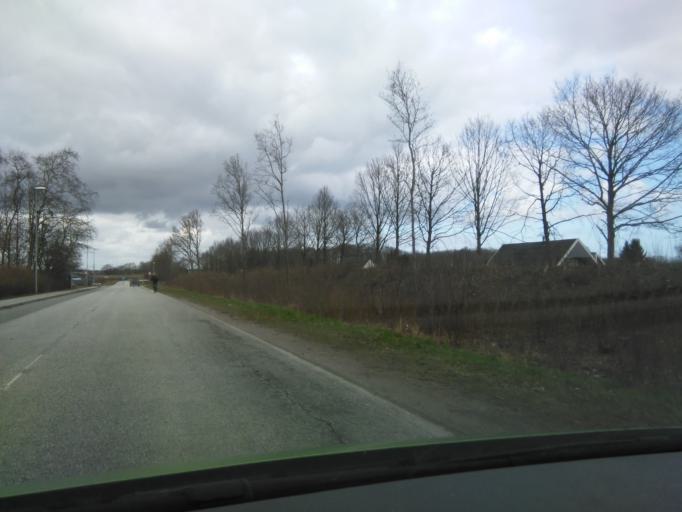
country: DK
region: Central Jutland
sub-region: Arhus Kommune
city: Malling
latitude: 56.0435
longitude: 10.1939
